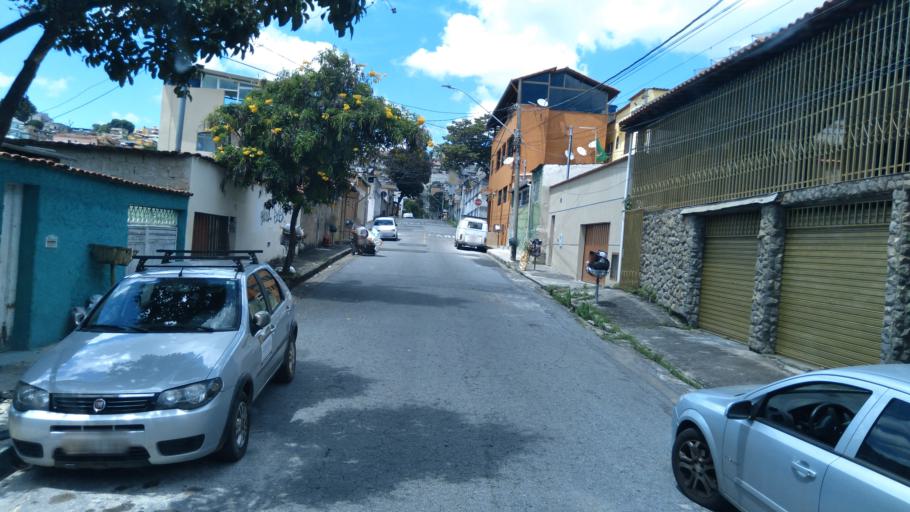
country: BR
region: Minas Gerais
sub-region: Belo Horizonte
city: Belo Horizonte
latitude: -19.8679
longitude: -43.9121
